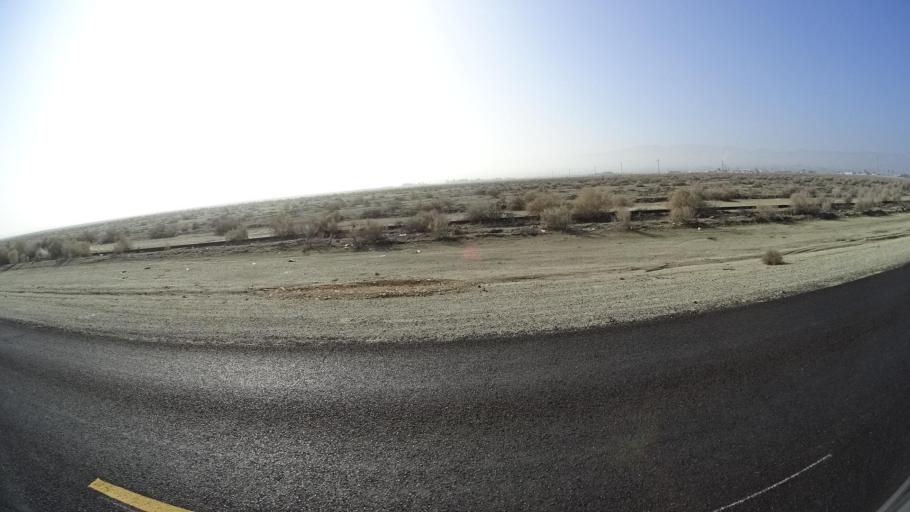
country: US
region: California
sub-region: Kern County
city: Taft Heights
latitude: 35.1805
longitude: -119.5078
